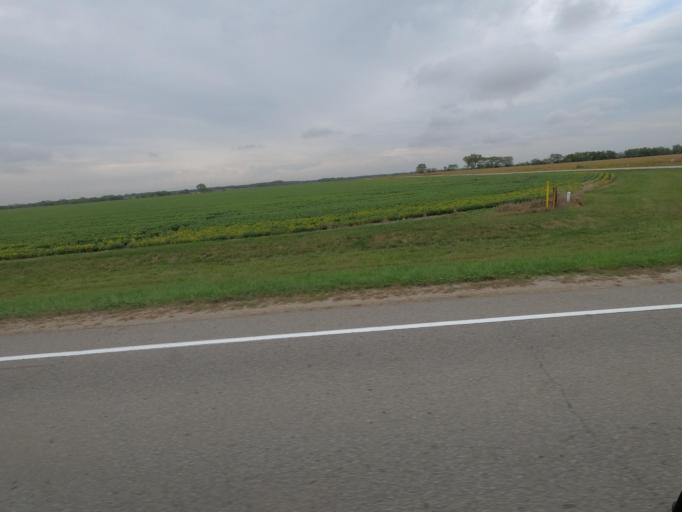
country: US
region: Iowa
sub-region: Van Buren County
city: Keosauqua
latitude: 40.8136
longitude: -91.8634
